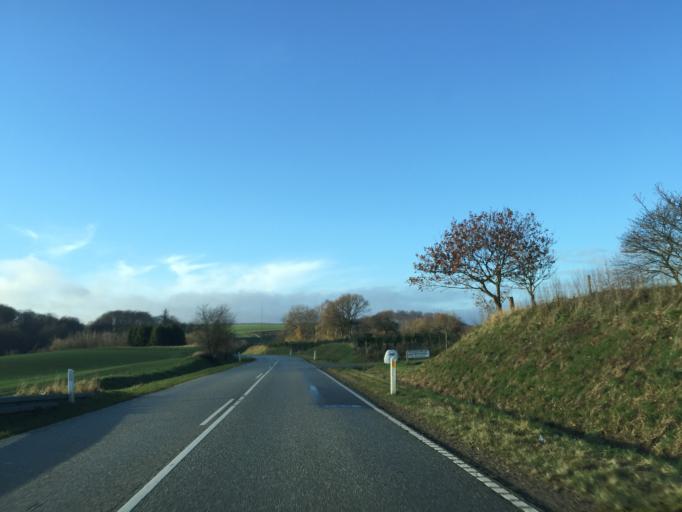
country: DK
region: Central Jutland
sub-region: Skanderborg Kommune
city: Galten
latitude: 56.1764
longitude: 9.8421
